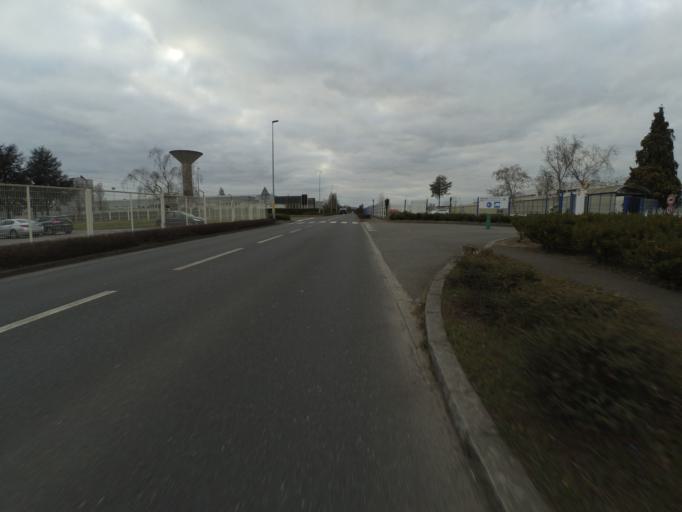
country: FR
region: Pays de la Loire
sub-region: Departement de la Loire-Atlantique
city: Sainte-Luce-sur-Loire
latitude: 47.2626
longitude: -1.5014
